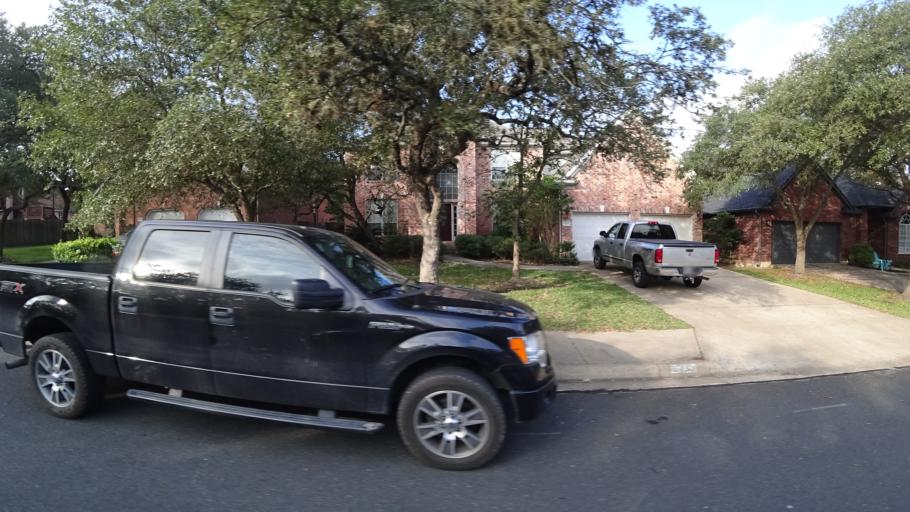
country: US
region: Texas
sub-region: Travis County
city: Shady Hollow
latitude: 30.1938
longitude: -97.8765
